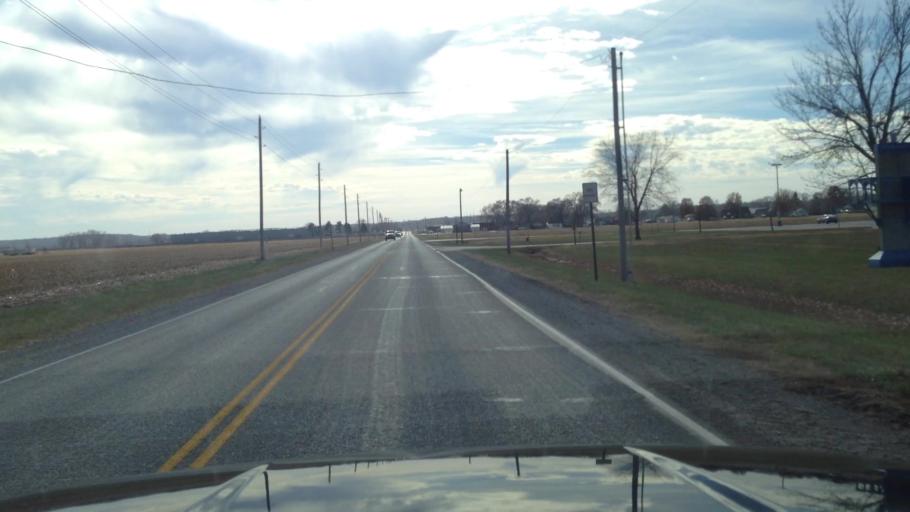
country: US
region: Kansas
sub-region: Jefferson County
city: Oskaloosa
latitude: 39.0777
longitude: -95.3820
